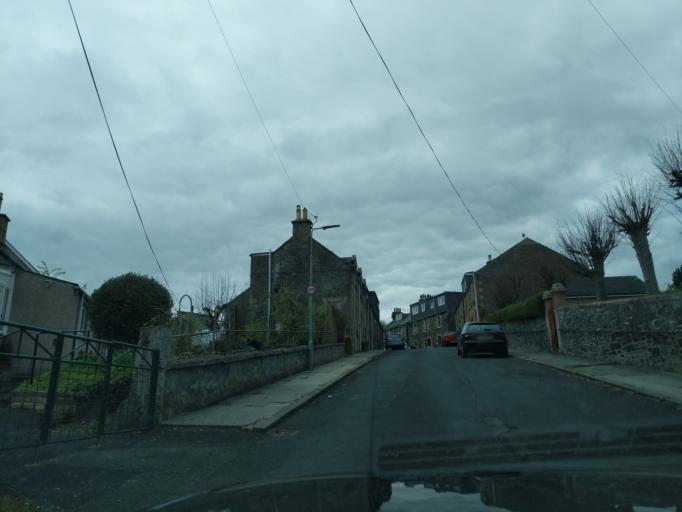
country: GB
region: Scotland
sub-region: The Scottish Borders
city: Selkirk
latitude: 55.5485
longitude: -2.8468
